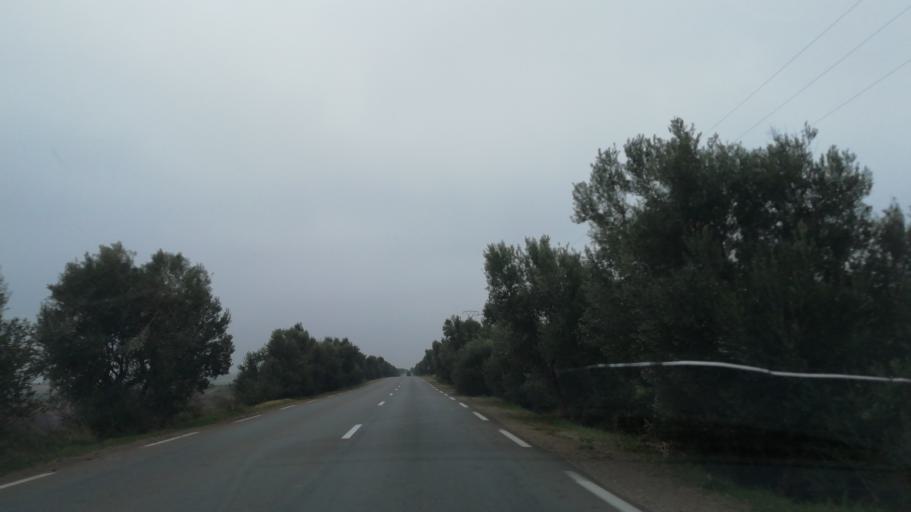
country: DZ
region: Mascara
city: Mascara
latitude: 35.3114
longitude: 0.3947
